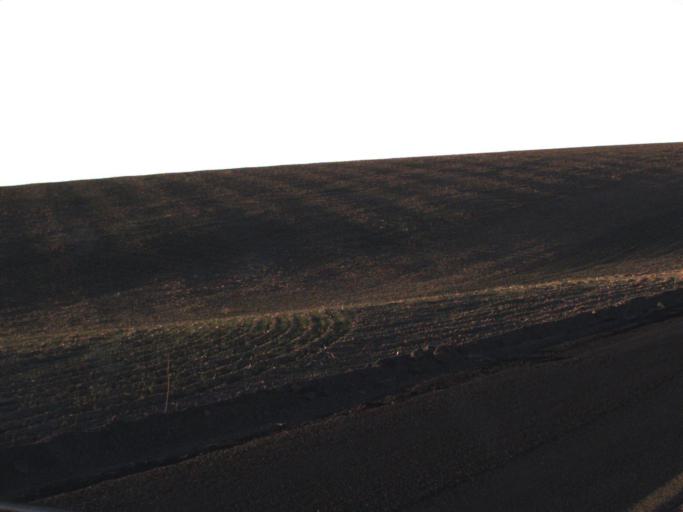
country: US
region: Washington
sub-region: Adams County
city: Ritzville
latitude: 46.9333
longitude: -118.5672
